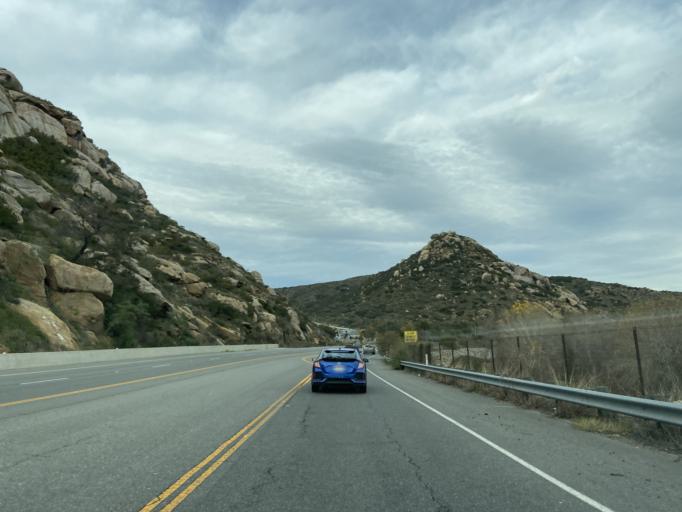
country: US
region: California
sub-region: San Diego County
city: Rainbow
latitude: 33.3390
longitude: -117.1434
